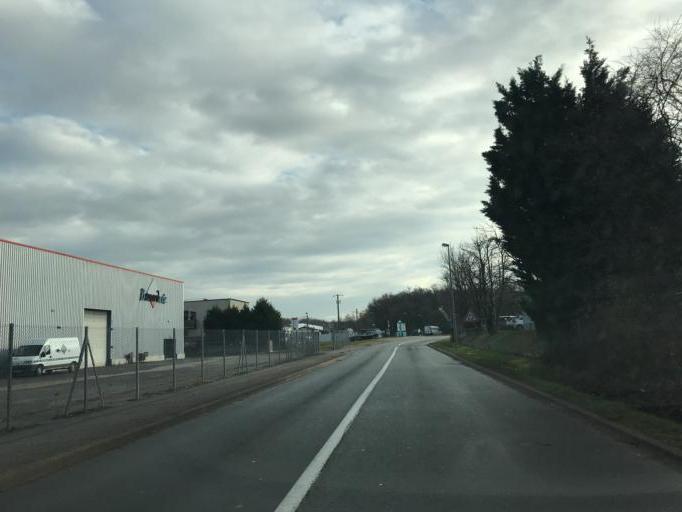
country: FR
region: Rhone-Alpes
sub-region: Departement de l'Ain
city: Reyrieux
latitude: 45.9435
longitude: 4.8157
